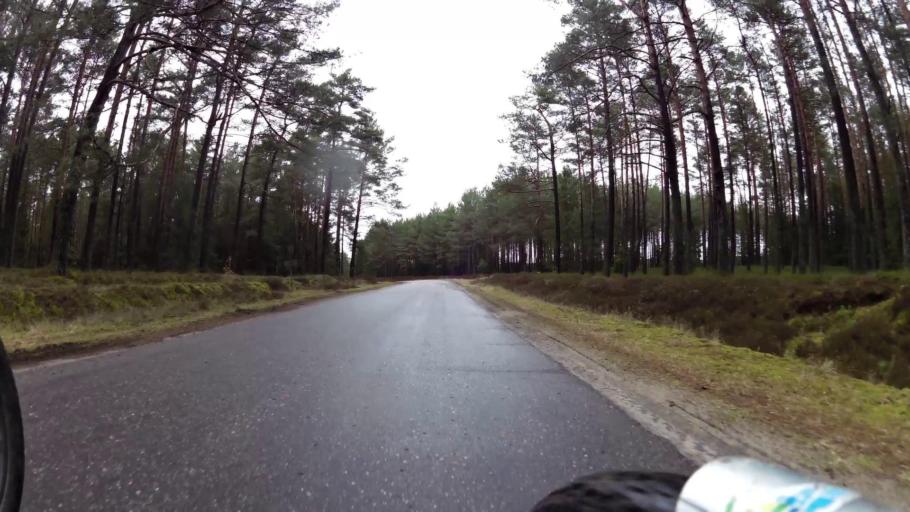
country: PL
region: Pomeranian Voivodeship
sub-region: Powiat bytowski
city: Borzytuchom
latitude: 54.2632
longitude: 17.3667
